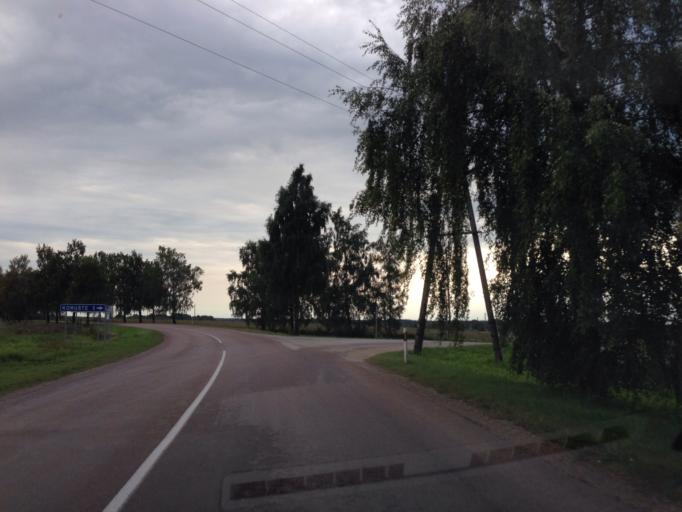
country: EE
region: Tartu
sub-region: Puhja vald
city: Puhja
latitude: 58.1774
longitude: 26.1972
